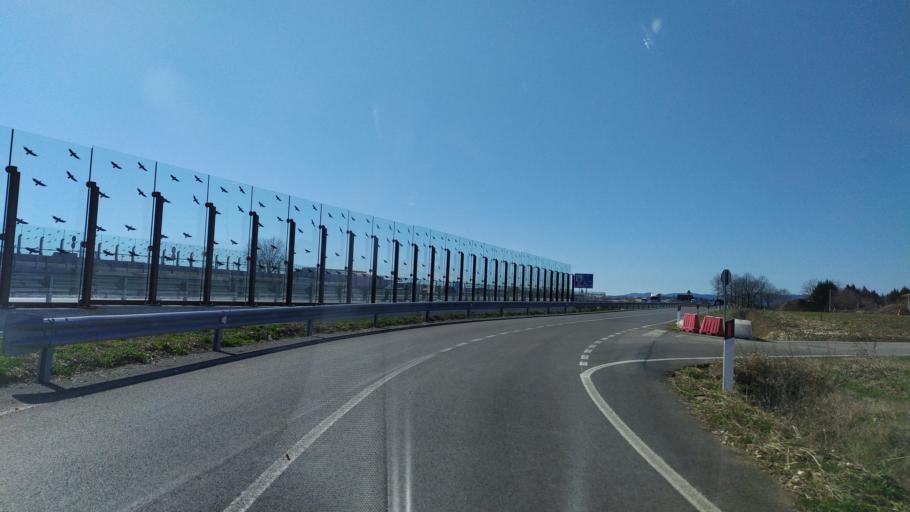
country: IT
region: Veneto
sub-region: Provincia di Vicenza
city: Mason Vicentino
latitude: 45.7035
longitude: 11.5990
